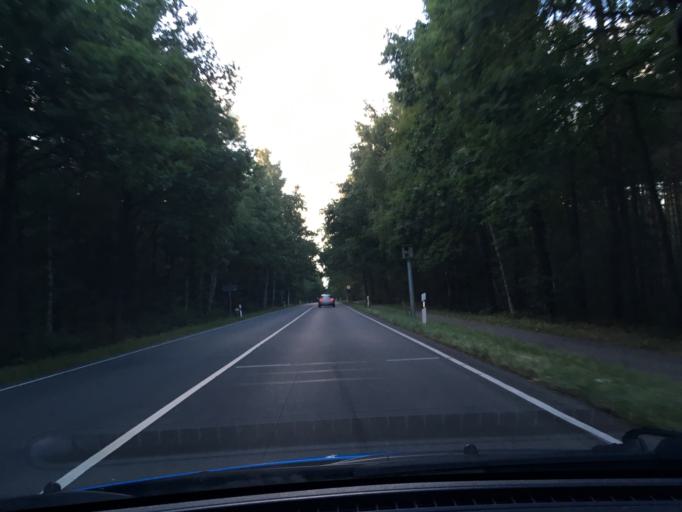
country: DE
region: Lower Saxony
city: Bergen
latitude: 52.7479
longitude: 9.9779
